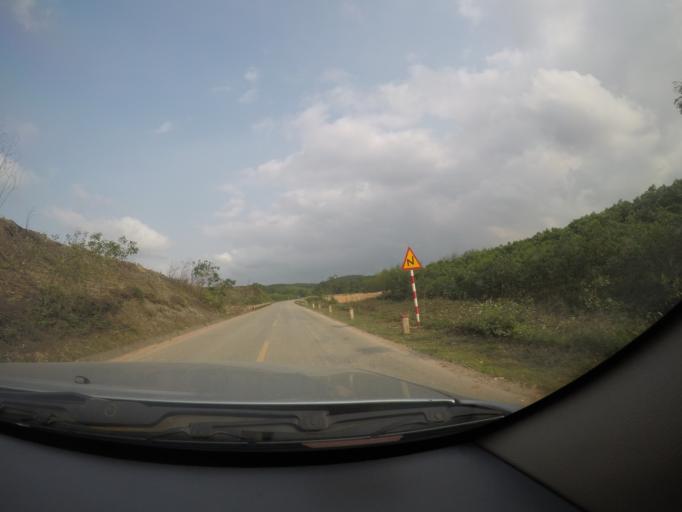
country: VN
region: Quang Binh
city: Kien Giang
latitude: 17.0962
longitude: 106.8501
